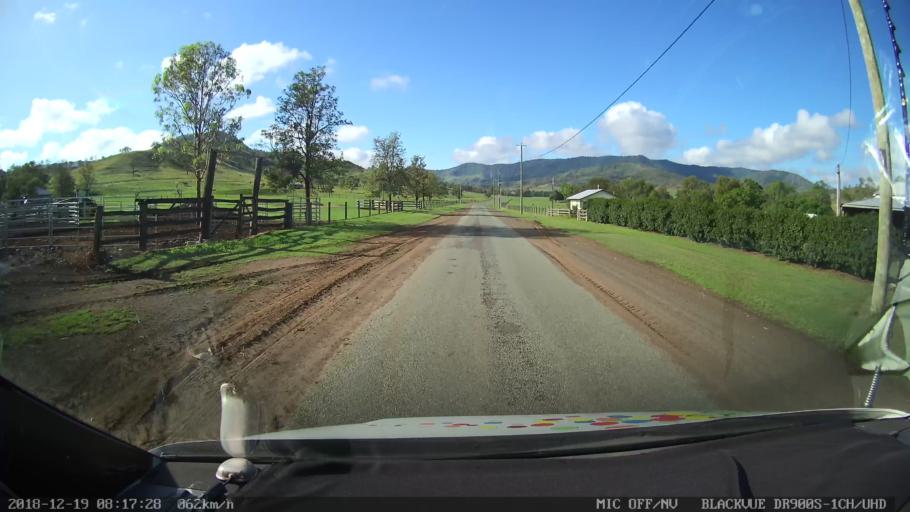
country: AU
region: New South Wales
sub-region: Kyogle
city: Kyogle
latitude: -28.2659
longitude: 152.9108
